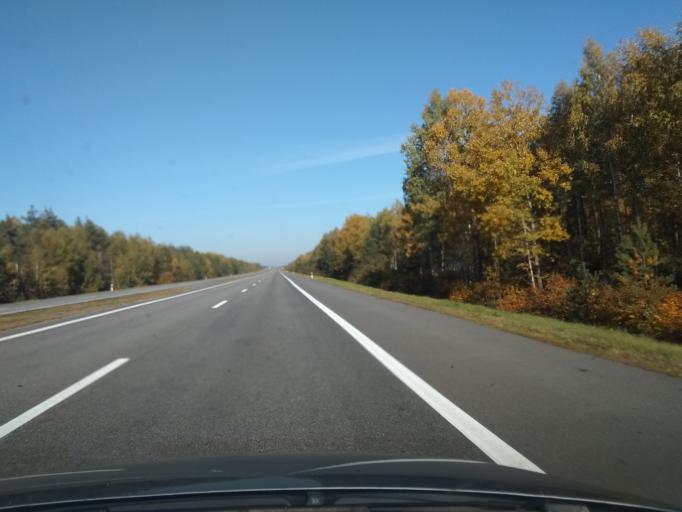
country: BY
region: Grodnenskaya
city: Zhyrovichy
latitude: 52.9001
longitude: 25.6750
